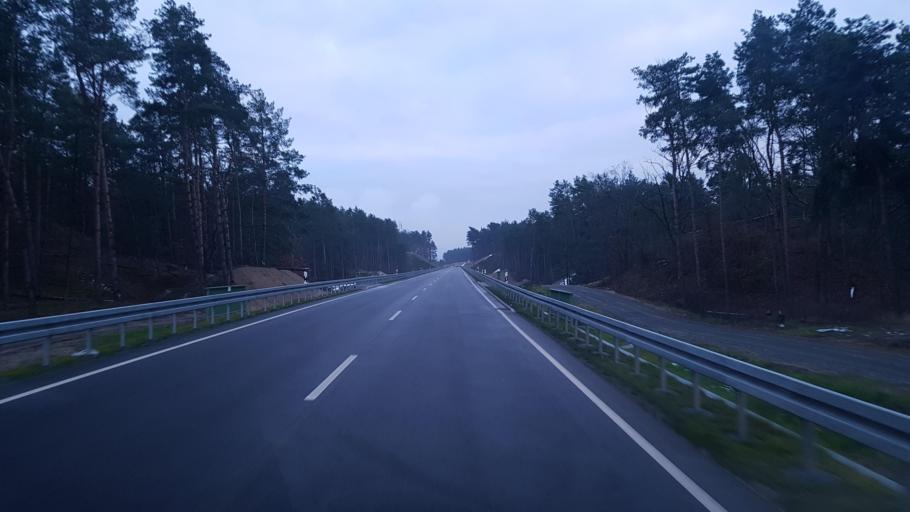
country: DE
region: Brandenburg
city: Wildau
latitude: 52.3216
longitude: 13.6573
